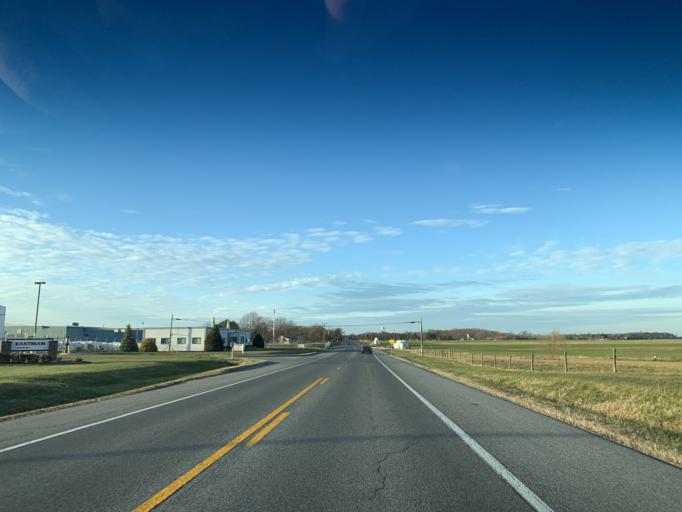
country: US
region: Maryland
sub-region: Kent County
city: Chestertown
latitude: 39.2620
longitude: -76.0862
